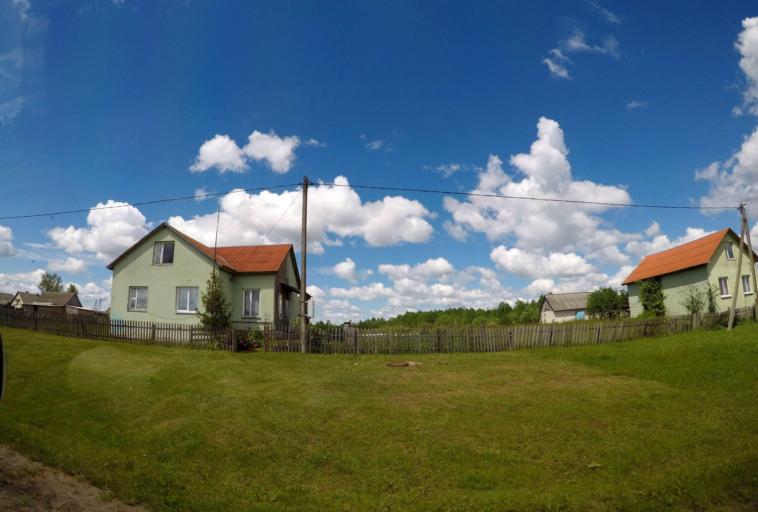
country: BY
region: Grodnenskaya
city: Hal'shany
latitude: 54.1678
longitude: 26.0950
